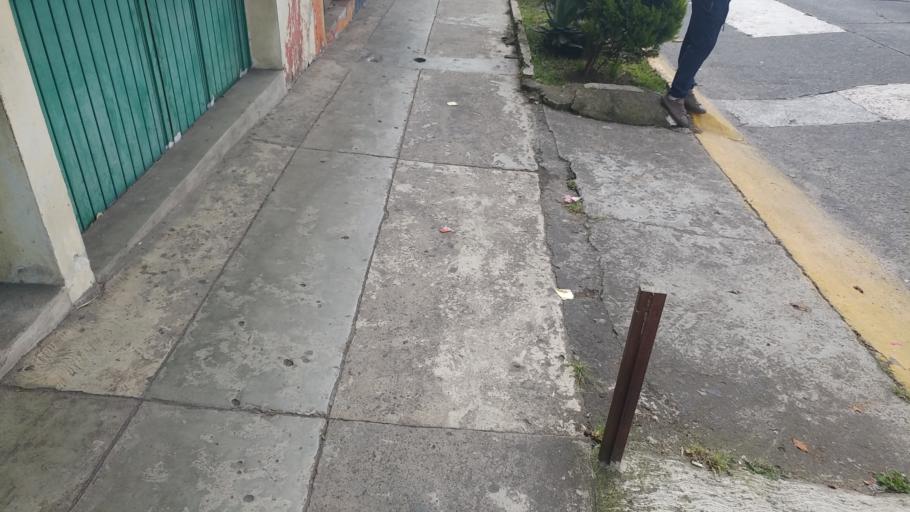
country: MX
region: Veracruz
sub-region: Xalapa
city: Xalapa de Enriquez
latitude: 19.5296
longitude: -96.9129
